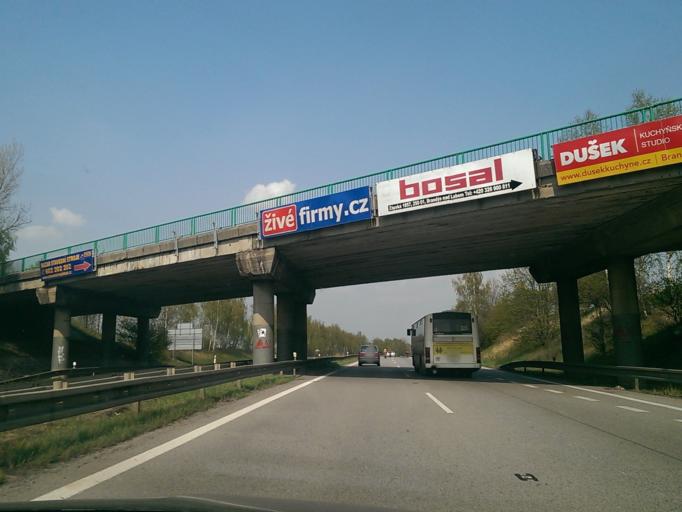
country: CZ
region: Central Bohemia
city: Brandys nad Labem-Stara Boleslav
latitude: 50.1695
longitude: 14.6739
